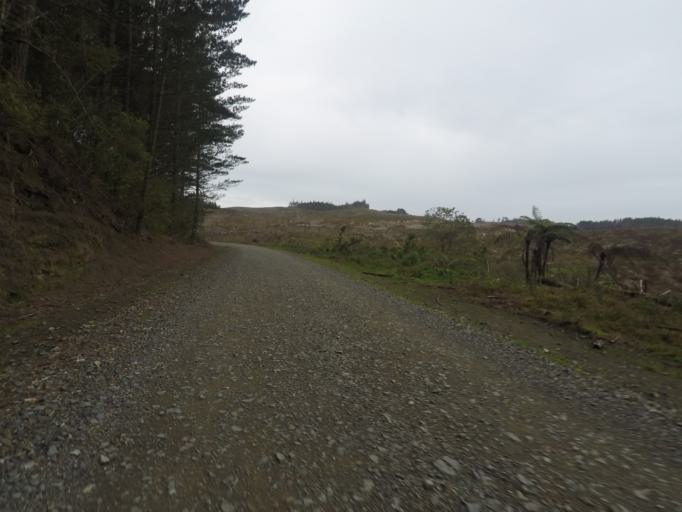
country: NZ
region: Auckland
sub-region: Auckland
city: Muriwai Beach
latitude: -36.7456
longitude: 174.5770
